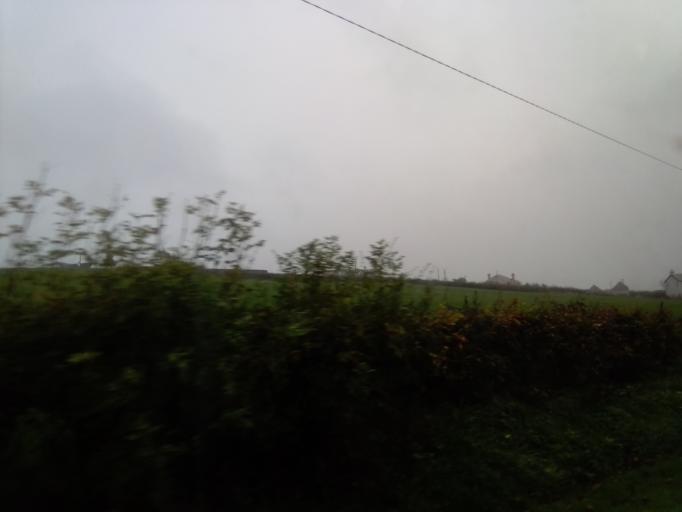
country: IE
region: Leinster
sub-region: Uibh Fhaili
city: Birr
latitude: 53.0368
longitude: -7.9009
